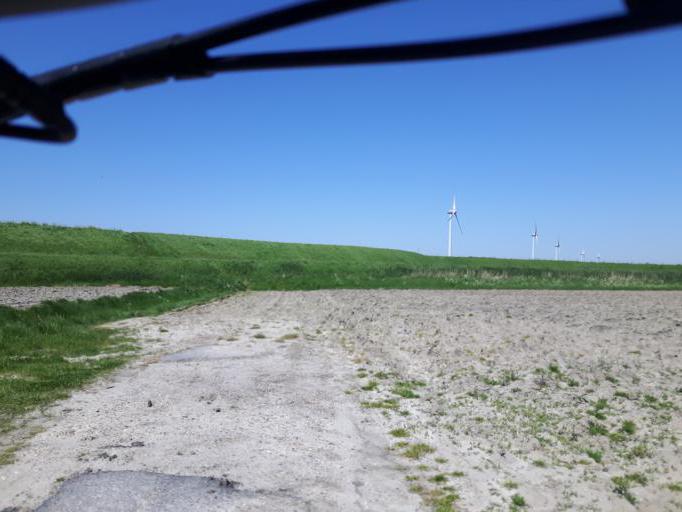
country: NL
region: Zeeland
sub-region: Gemeente Reimerswaal
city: Yerseke
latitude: 51.5512
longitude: 4.0521
